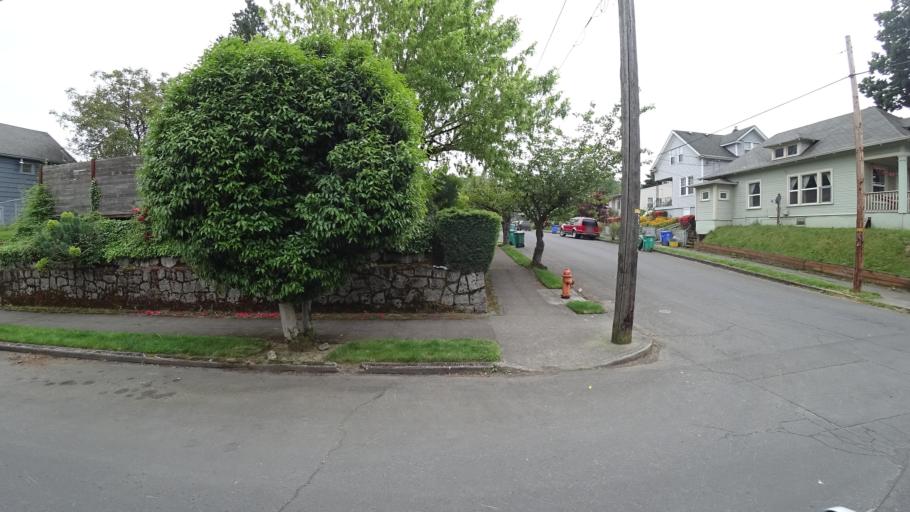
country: US
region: Oregon
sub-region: Multnomah County
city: Portland
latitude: 45.5495
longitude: -122.6566
